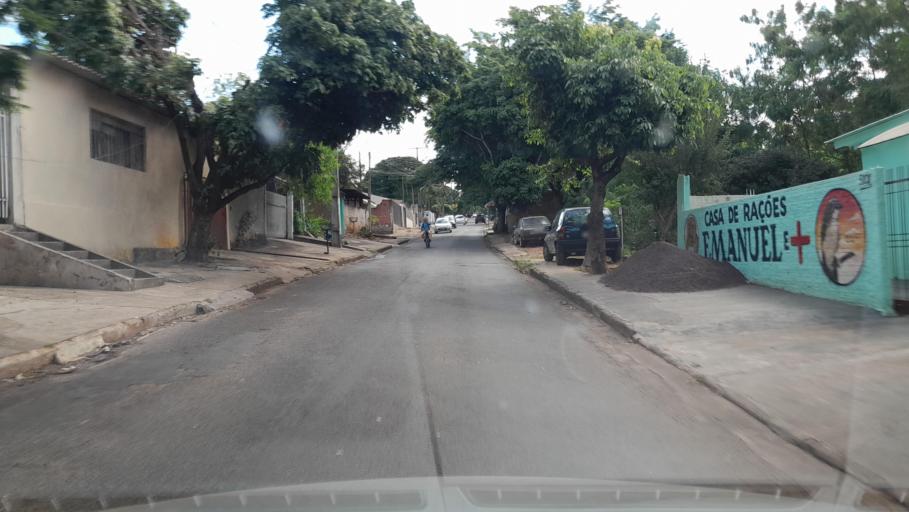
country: BR
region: Parana
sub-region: Umuarama
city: Umuarama
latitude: -23.7724
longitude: -53.3052
